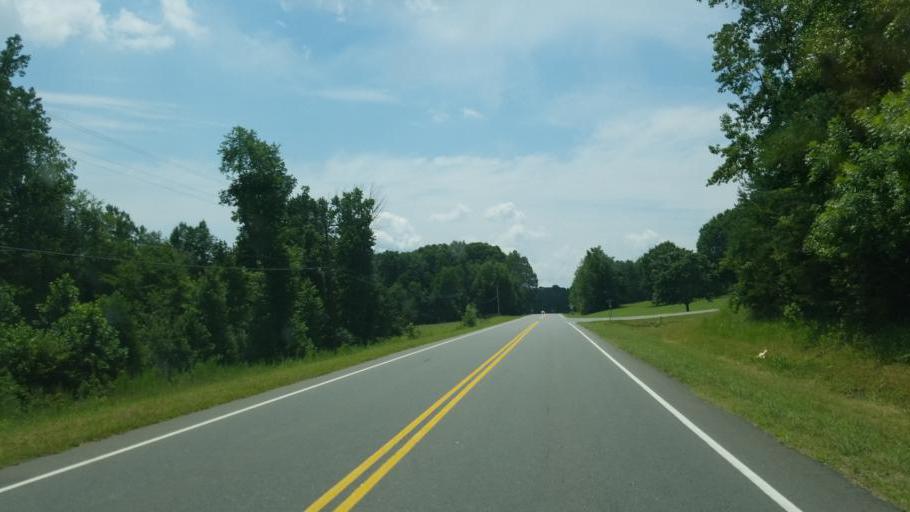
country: US
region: North Carolina
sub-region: Cleveland County
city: Kings Mountain
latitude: 35.1993
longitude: -81.3410
